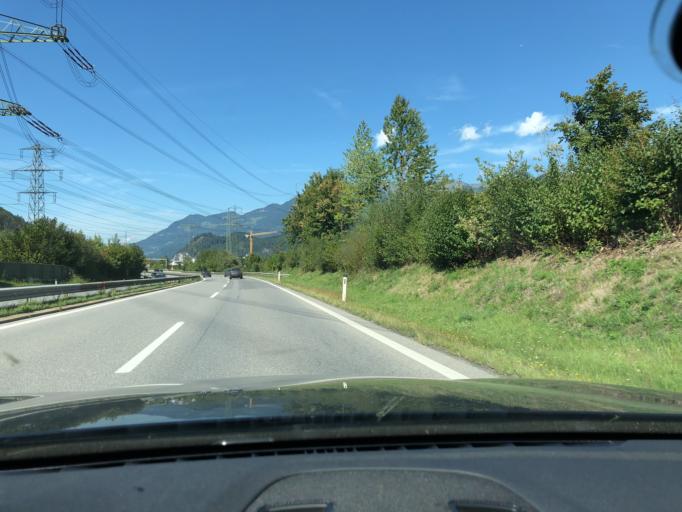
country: AT
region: Vorarlberg
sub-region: Politischer Bezirk Bludenz
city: Buers
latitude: 47.1561
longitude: 9.8071
